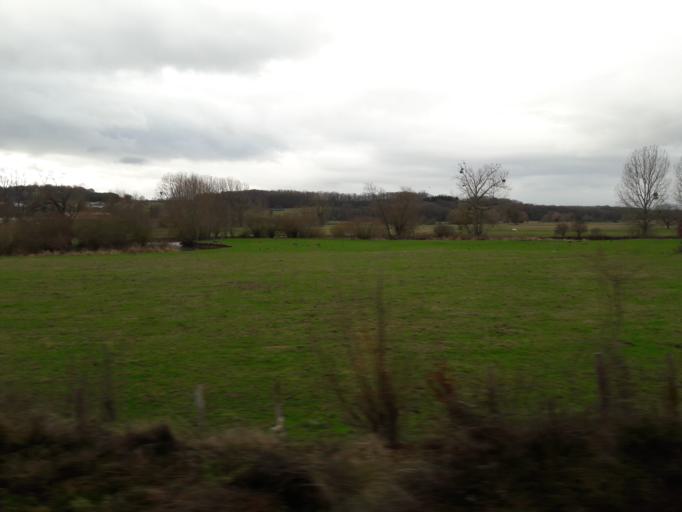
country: FR
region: Franche-Comte
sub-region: Territoire de Belfort
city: Joncherey
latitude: 47.5300
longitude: 6.9965
